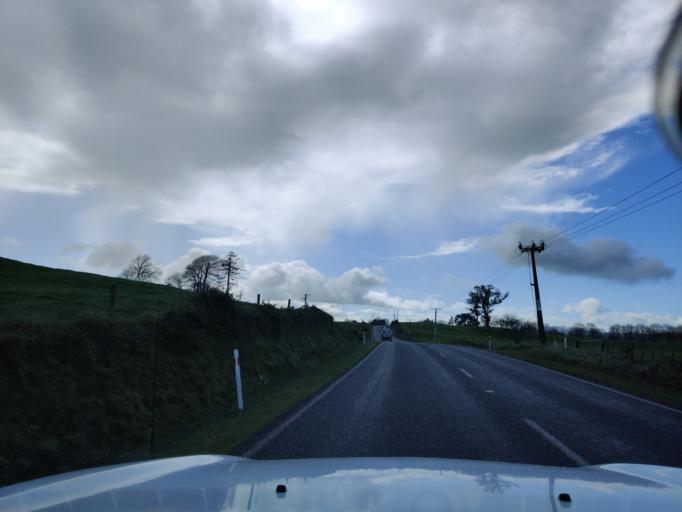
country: NZ
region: Waikato
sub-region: Waikato District
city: Ngaruawahia
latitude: -37.5754
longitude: 175.2390
